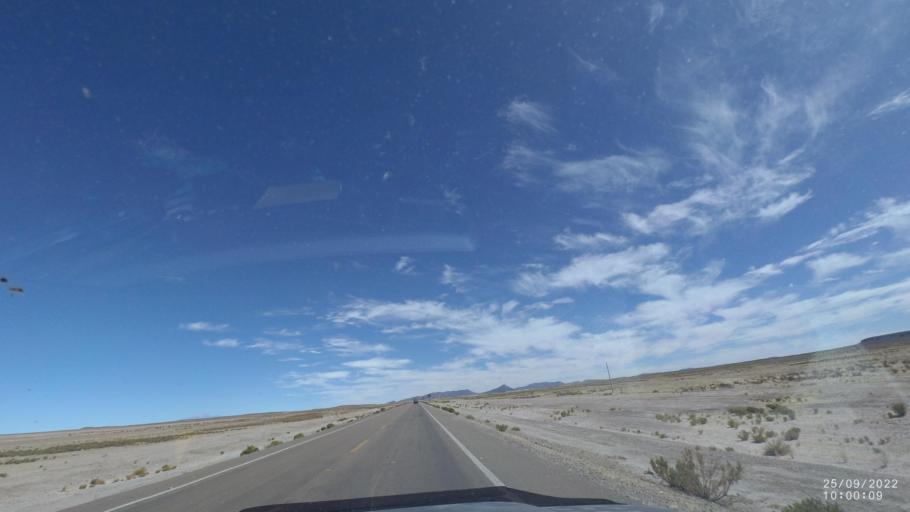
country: BO
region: Potosi
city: Colchani
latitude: -20.2787
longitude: -66.9445
